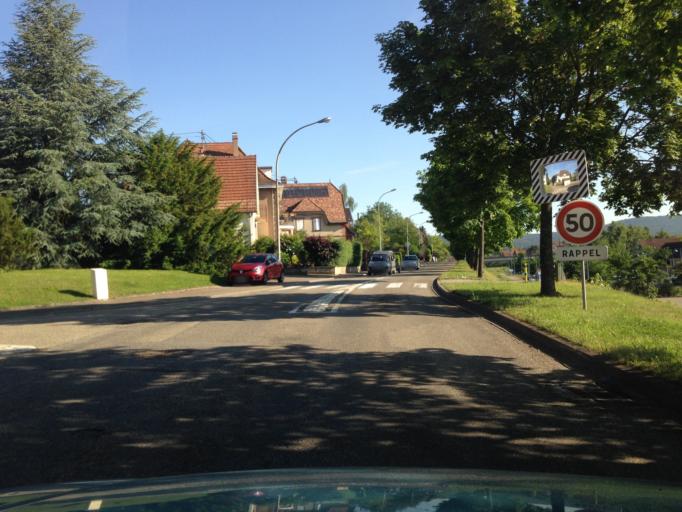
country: FR
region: Alsace
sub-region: Departement du Bas-Rhin
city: Ingwiller
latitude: 48.8709
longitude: 7.4762
